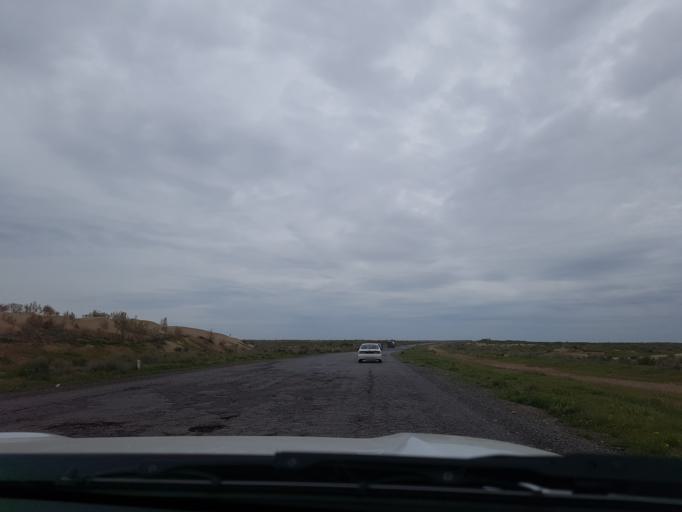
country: TM
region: Mary
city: Bayramaly
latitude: 38.0347
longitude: 62.7529
